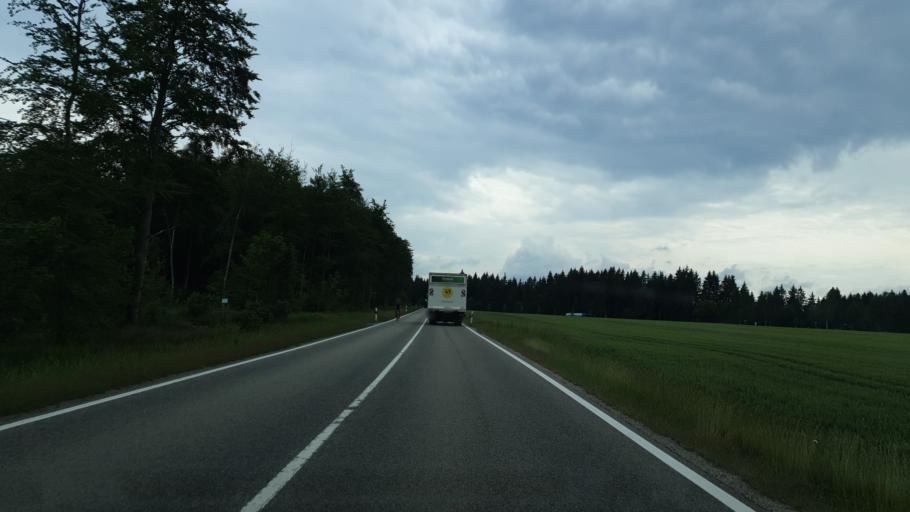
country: DE
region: Saxony
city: Hammerbrucke
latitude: 50.4739
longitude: 12.4322
